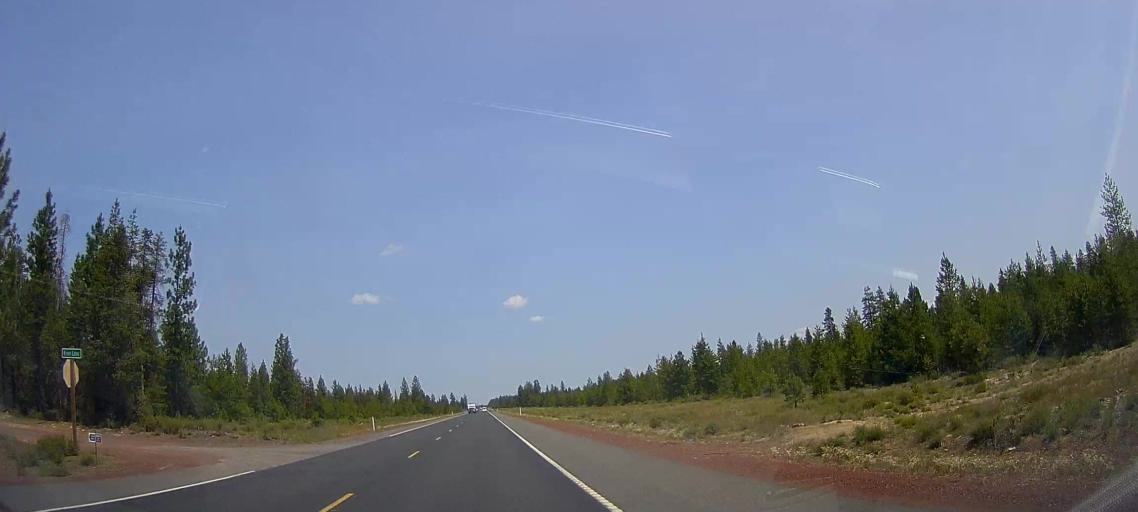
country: US
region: Oregon
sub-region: Deschutes County
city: La Pine
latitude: 43.4961
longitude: -121.6733
